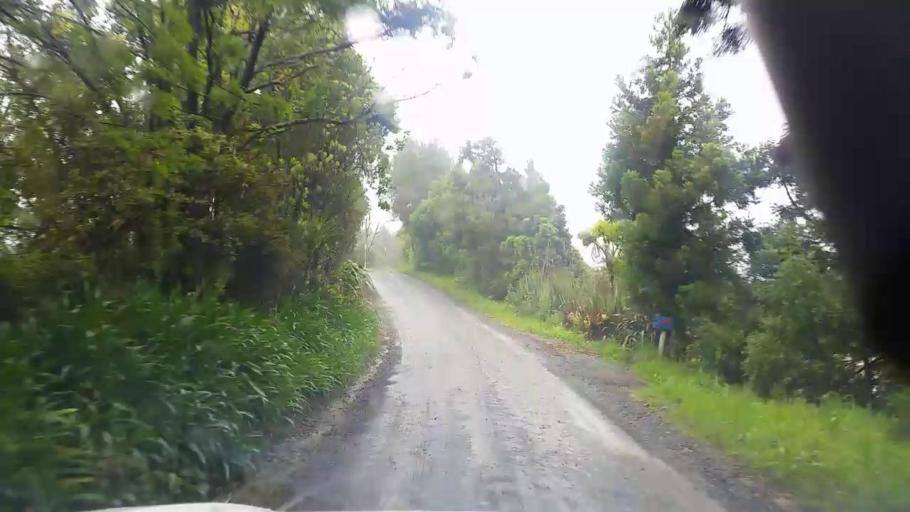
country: NZ
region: Auckland
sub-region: Auckland
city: Muriwai Beach
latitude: -36.8460
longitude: 174.5103
